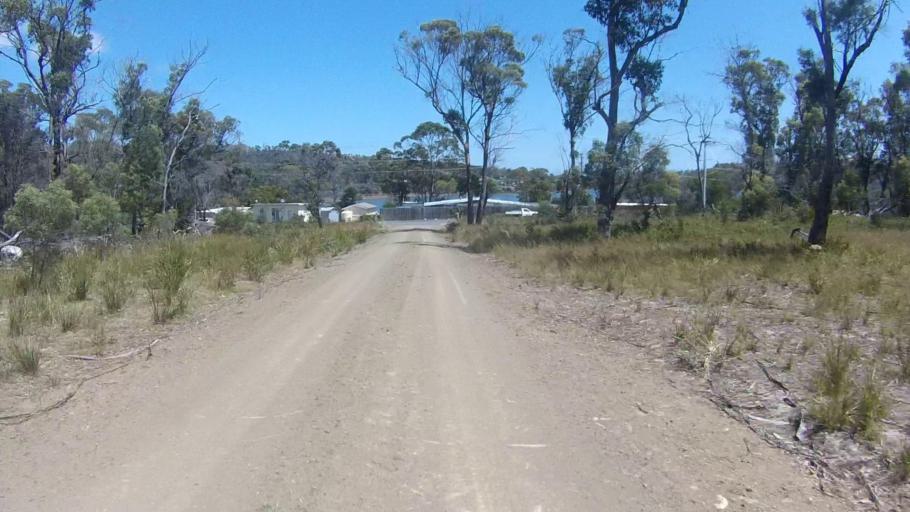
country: AU
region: Tasmania
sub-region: Sorell
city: Sorell
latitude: -42.9444
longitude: 147.8663
